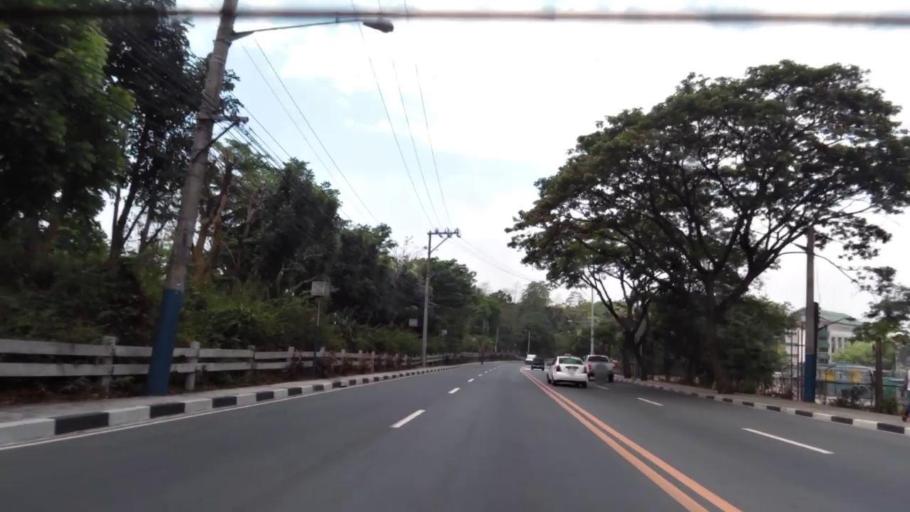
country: PH
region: Calabarzon
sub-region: Province of Rizal
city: Antipolo
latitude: 14.6190
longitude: 121.1503
